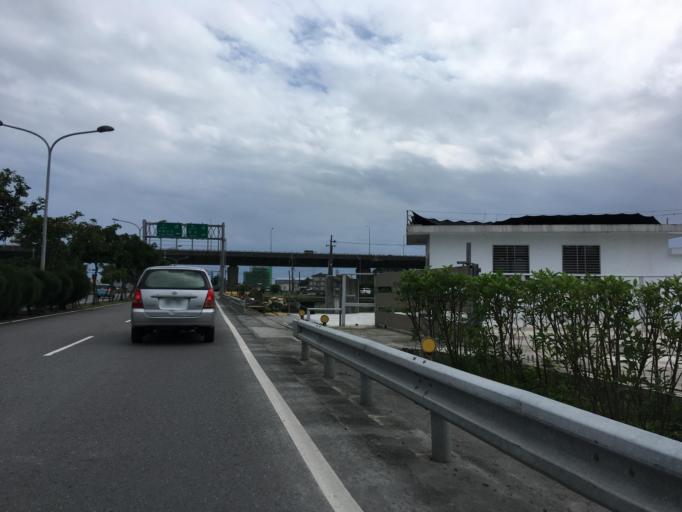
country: TW
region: Taiwan
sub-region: Yilan
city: Yilan
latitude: 24.6796
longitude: 121.7917
